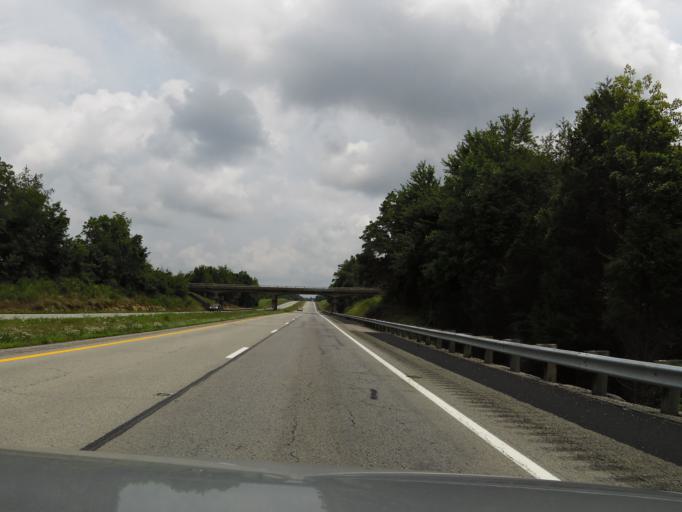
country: US
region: Kentucky
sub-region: Grayson County
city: Leitchfield
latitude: 37.5353
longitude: -86.1367
